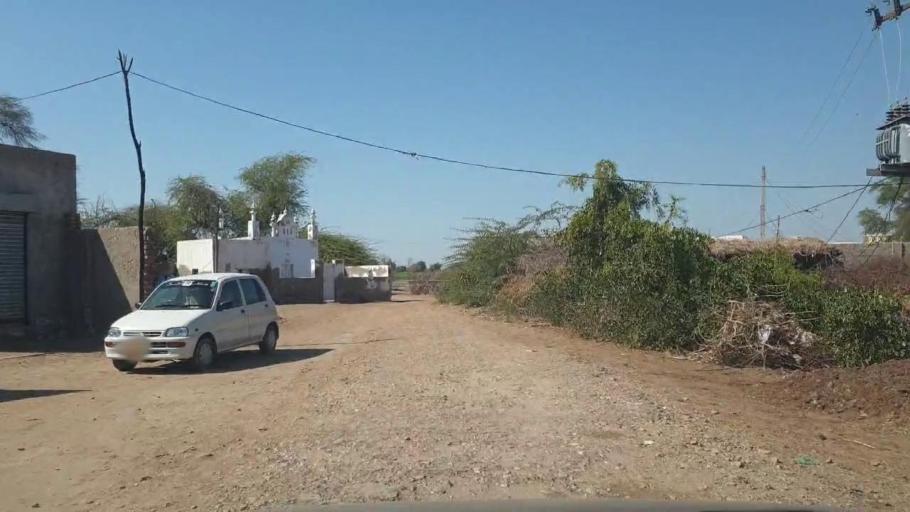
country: PK
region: Sindh
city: Dhoro Naro
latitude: 25.3981
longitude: 69.6083
